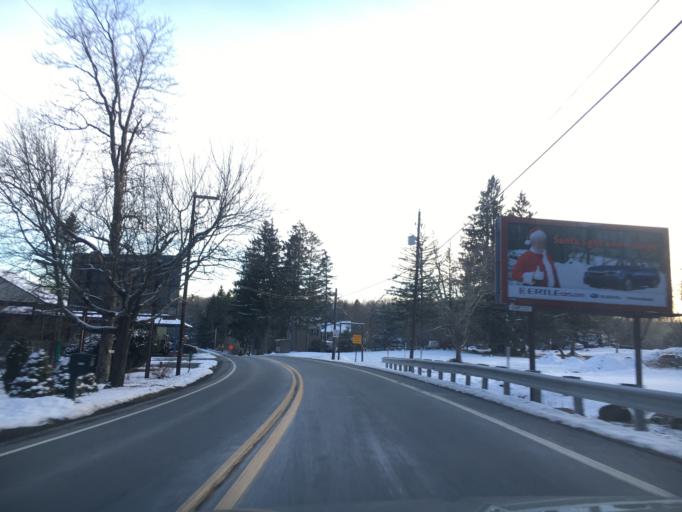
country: US
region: Pennsylvania
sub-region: Pike County
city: Hemlock Farms
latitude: 41.2856
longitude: -75.0929
